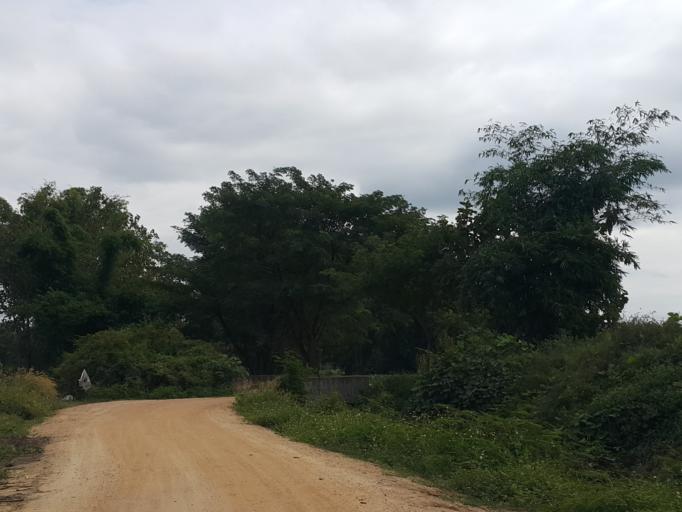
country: TH
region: Lampang
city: Hang Chat
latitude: 18.4747
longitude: 99.4142
